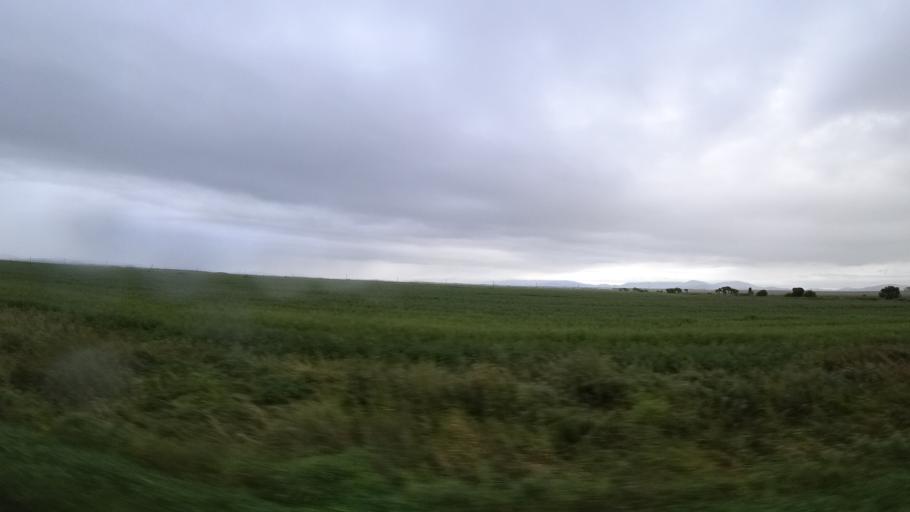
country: RU
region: Primorskiy
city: Chernigovka
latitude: 44.3833
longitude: 132.5296
